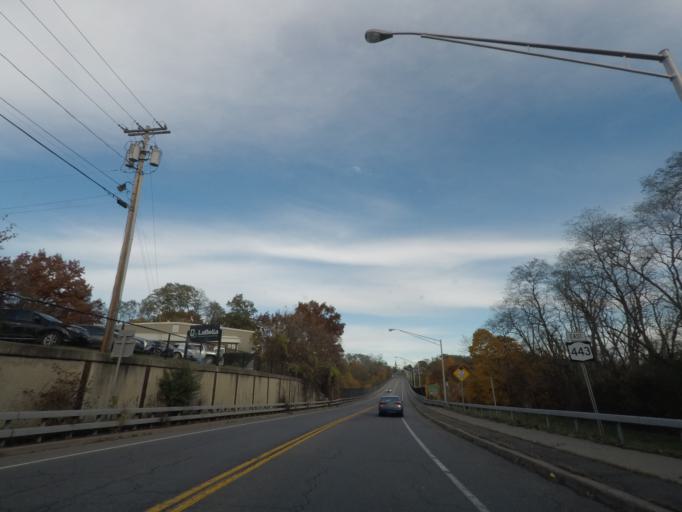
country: US
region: New York
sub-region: Albany County
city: Delmar
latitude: 42.6332
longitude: -73.8014
